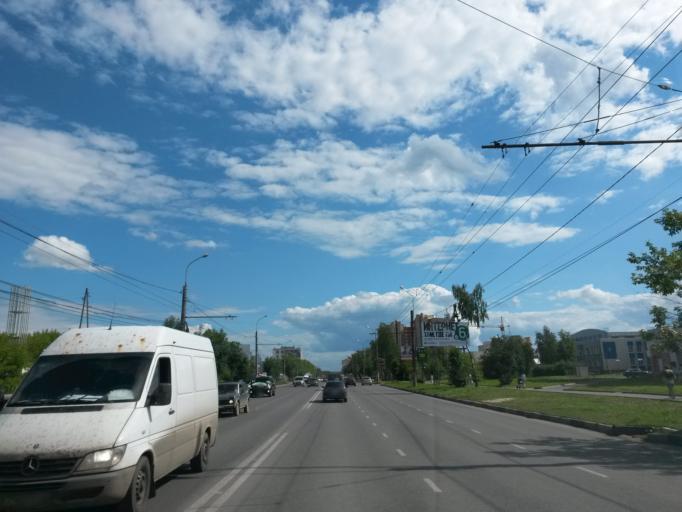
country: RU
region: Ivanovo
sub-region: Gorod Ivanovo
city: Ivanovo
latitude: 56.9688
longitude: 41.0167
